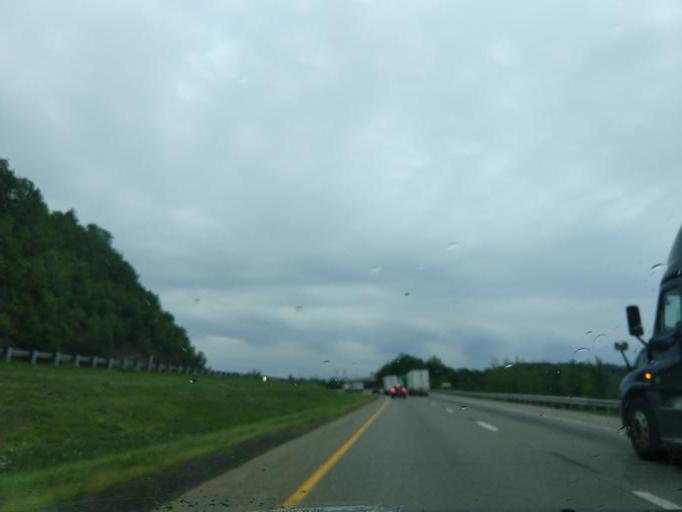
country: US
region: Pennsylvania
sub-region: Luzerne County
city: Conyngham
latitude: 40.9856
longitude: -76.0335
